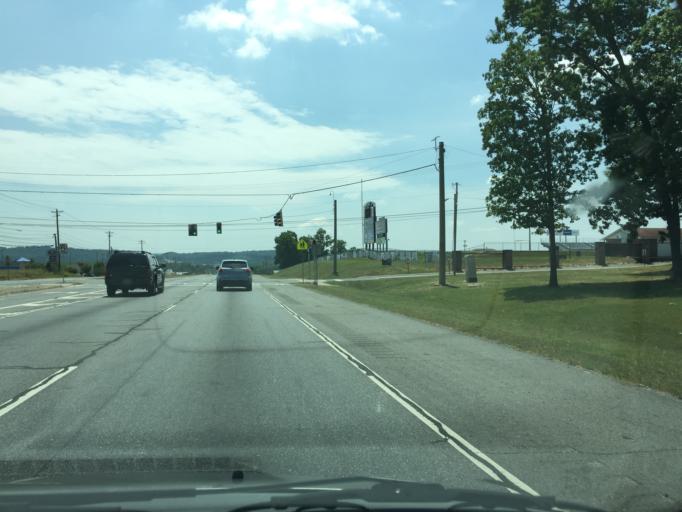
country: US
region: Georgia
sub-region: Catoosa County
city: Fort Oglethorpe
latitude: 34.9479
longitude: -85.2343
